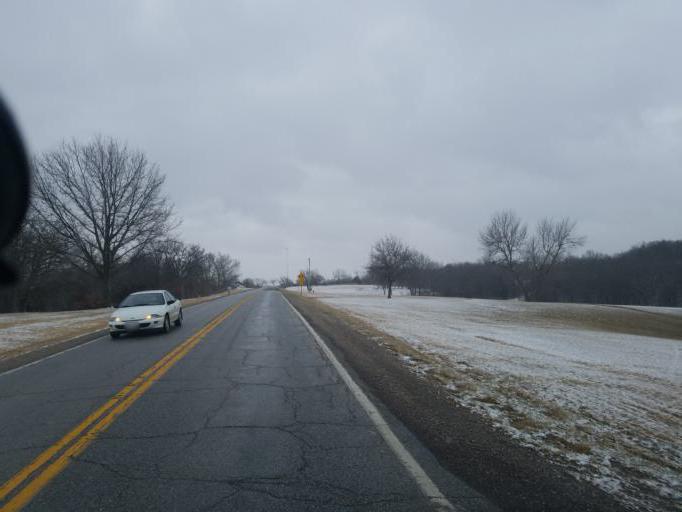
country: US
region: Missouri
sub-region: Putnam County
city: Unionville
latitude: 40.5241
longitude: -93.0133
